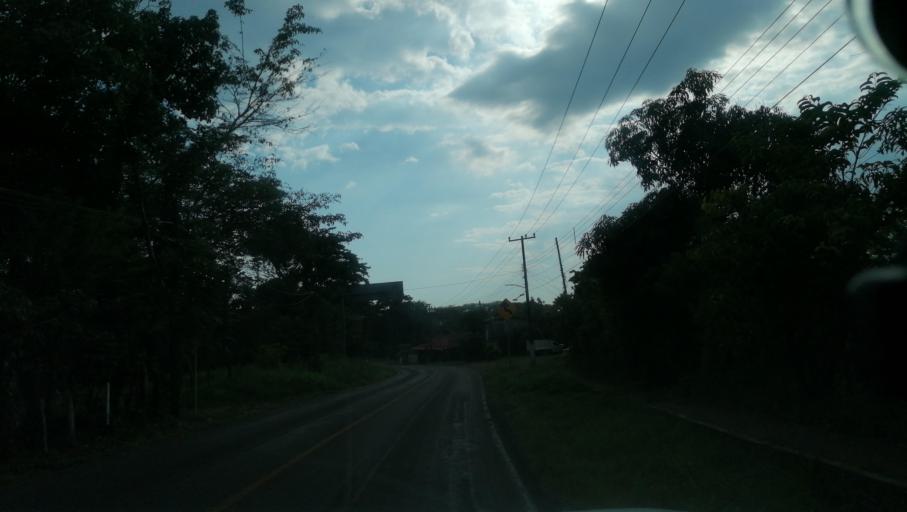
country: MX
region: Chiapas
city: Cacahoatan
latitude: 15.0047
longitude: -92.1568
